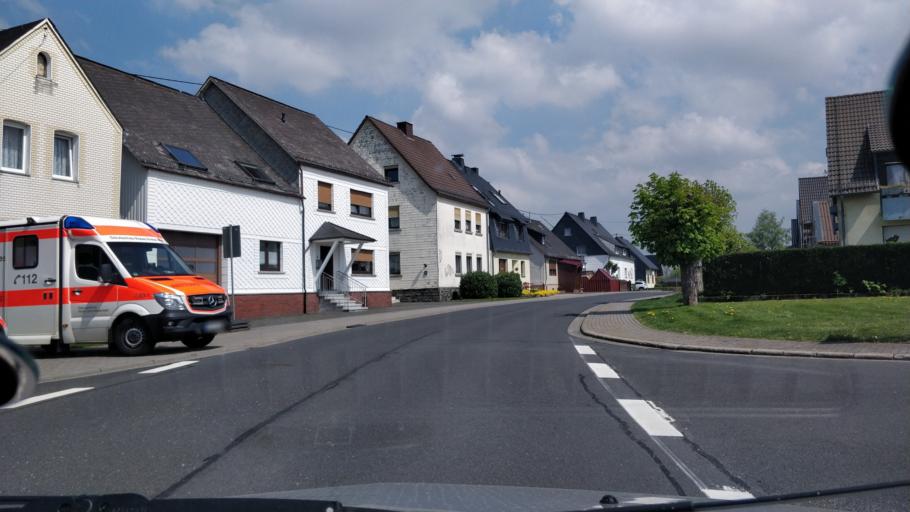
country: DE
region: Rheinland-Pfalz
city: Hohn
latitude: 50.6203
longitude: 7.9875
